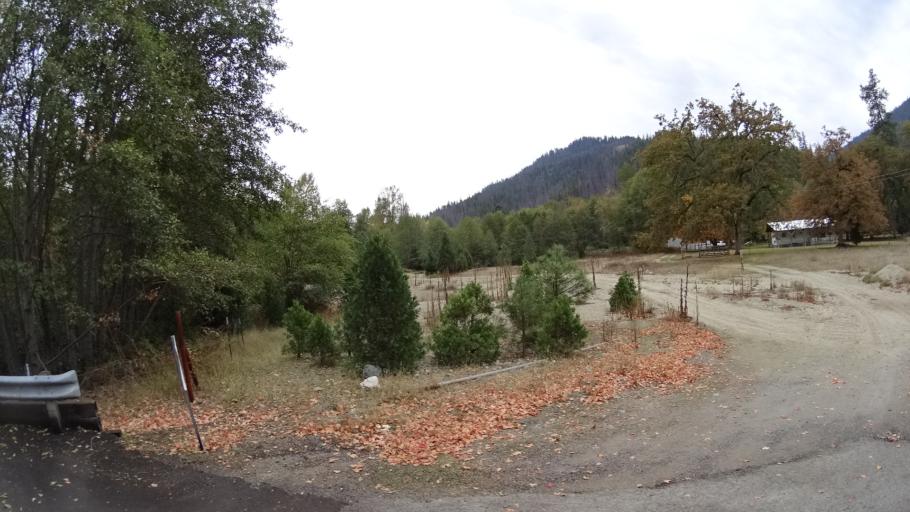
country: US
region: California
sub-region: Siskiyou County
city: Happy Camp
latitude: 41.8375
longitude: -123.2081
